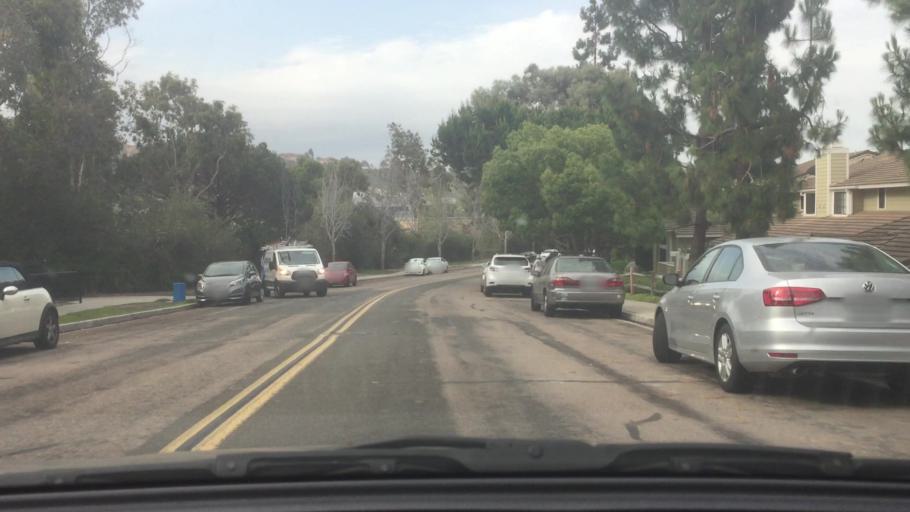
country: US
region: California
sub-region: San Diego County
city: Del Mar
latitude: 32.9400
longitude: -117.2329
